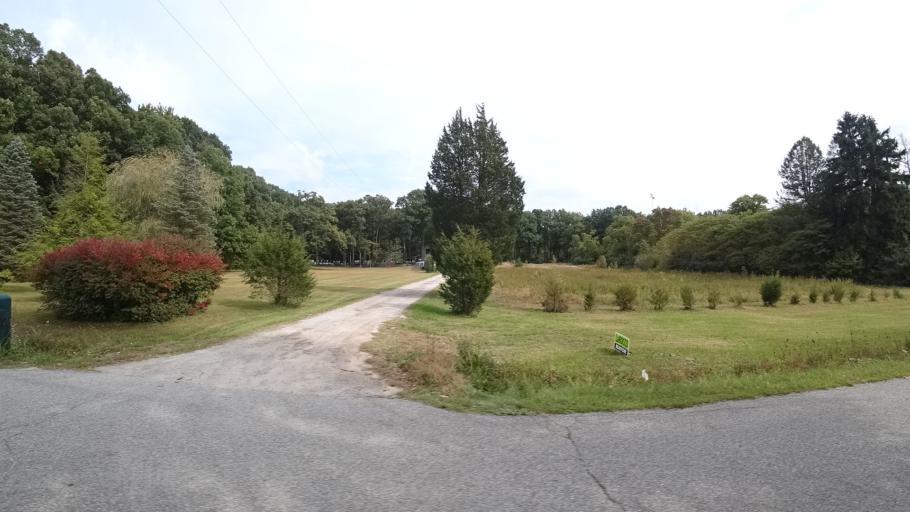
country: US
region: Indiana
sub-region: LaPorte County
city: Trail Creek
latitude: 41.7132
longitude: -86.8163
